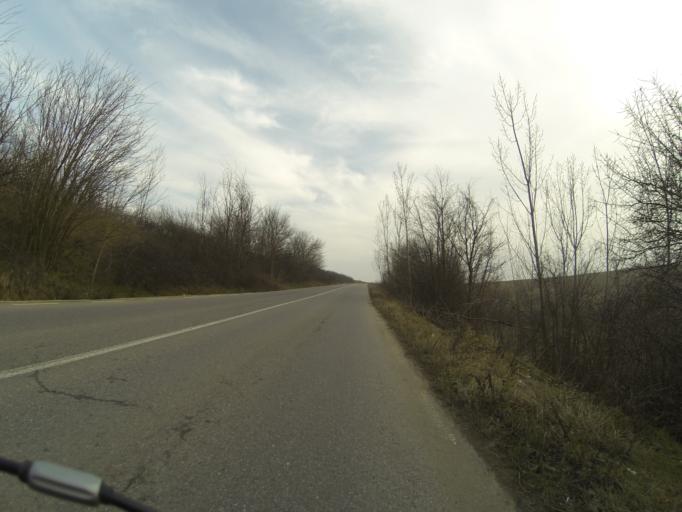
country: RO
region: Mehedinti
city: Vanju-Mare
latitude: 44.4110
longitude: 22.8846
